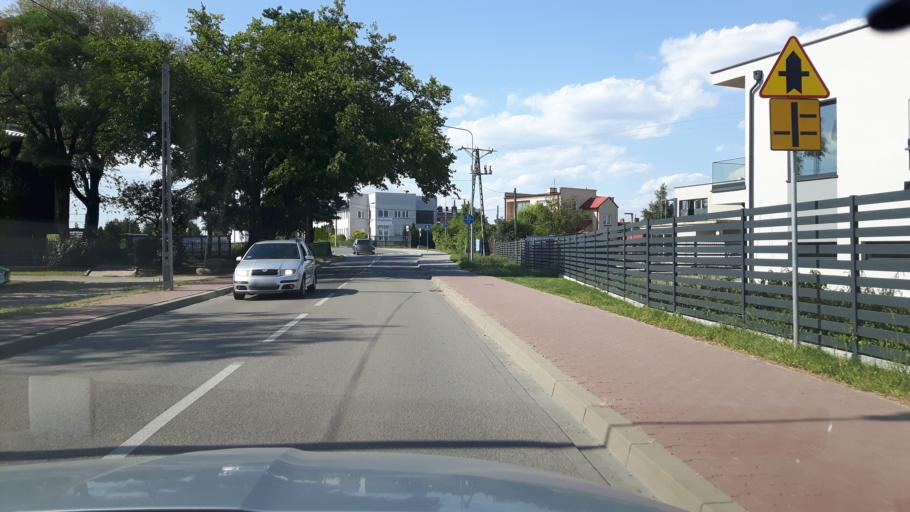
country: PL
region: Masovian Voivodeship
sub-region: Powiat pruszkowski
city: Nowe Grocholice
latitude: 52.1635
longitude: 20.9114
